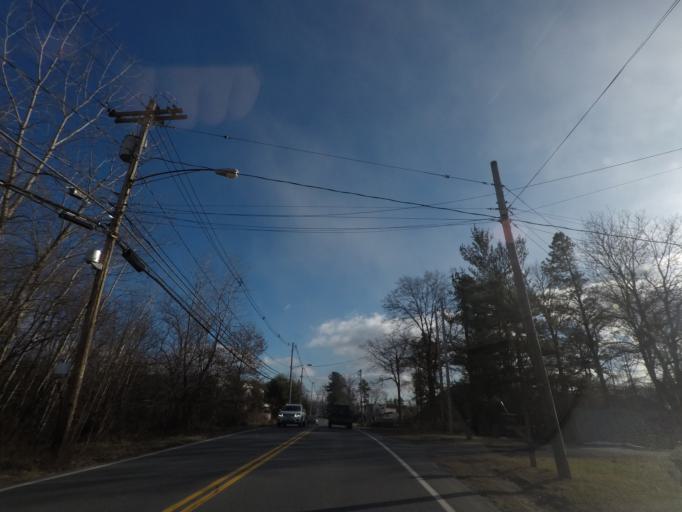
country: US
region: New York
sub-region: Albany County
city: Colonie
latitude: 42.7313
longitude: -73.8630
